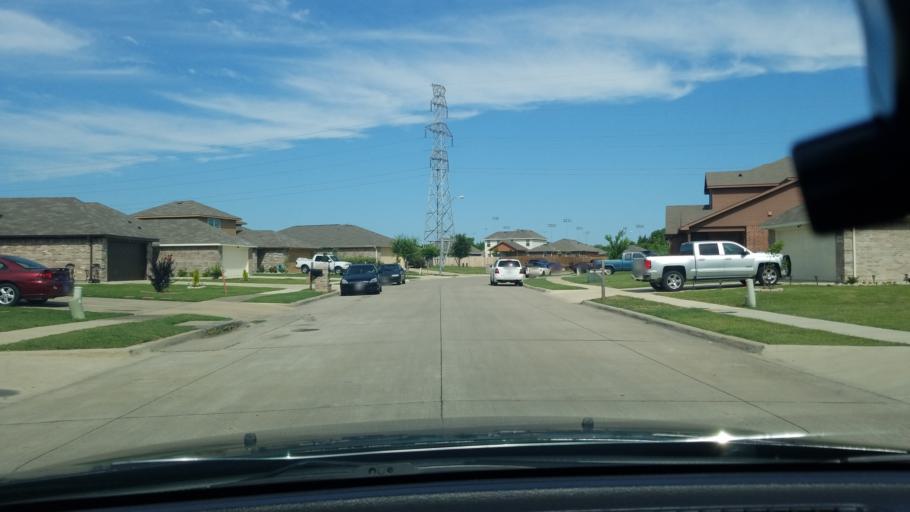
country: US
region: Texas
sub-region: Dallas County
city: Balch Springs
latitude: 32.7700
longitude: -96.6714
